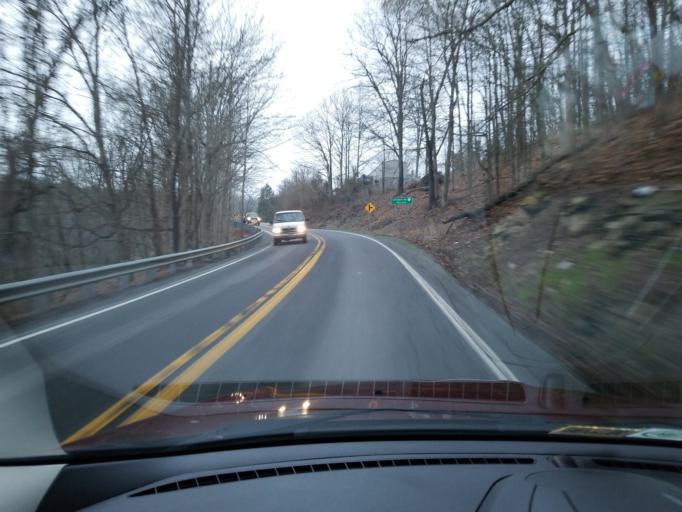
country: US
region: West Virginia
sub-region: Monroe County
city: Union
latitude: 37.5681
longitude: -80.5701
